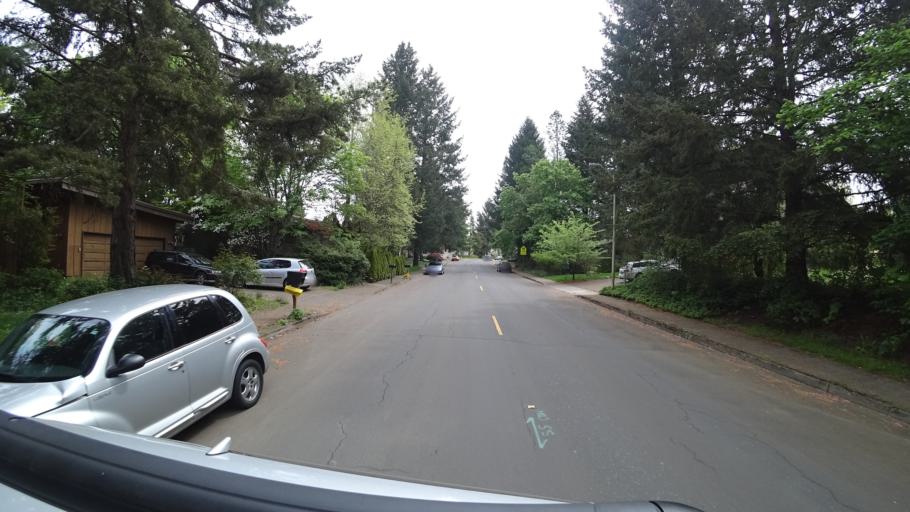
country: US
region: Oregon
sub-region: Washington County
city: Hillsboro
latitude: 45.5302
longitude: -122.9985
